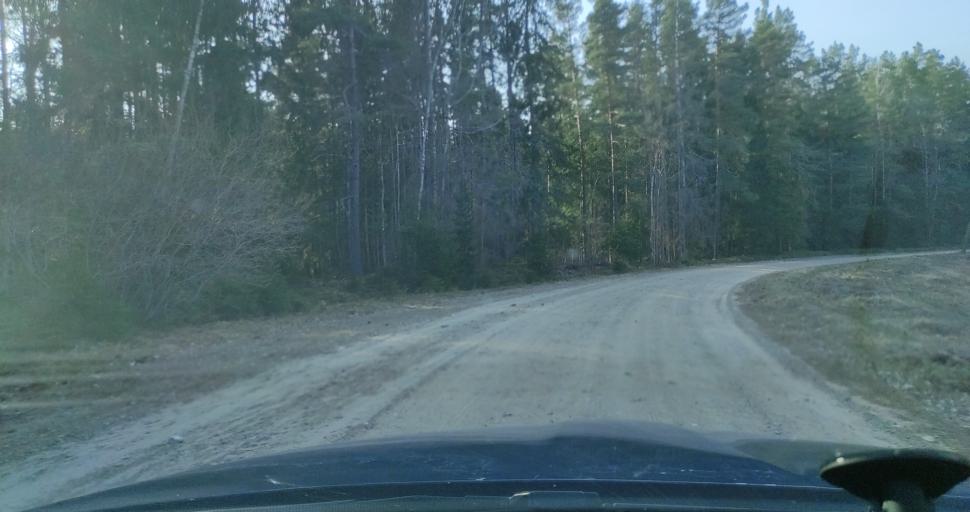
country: LV
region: Kuldigas Rajons
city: Kuldiga
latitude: 57.0173
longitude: 22.0129
